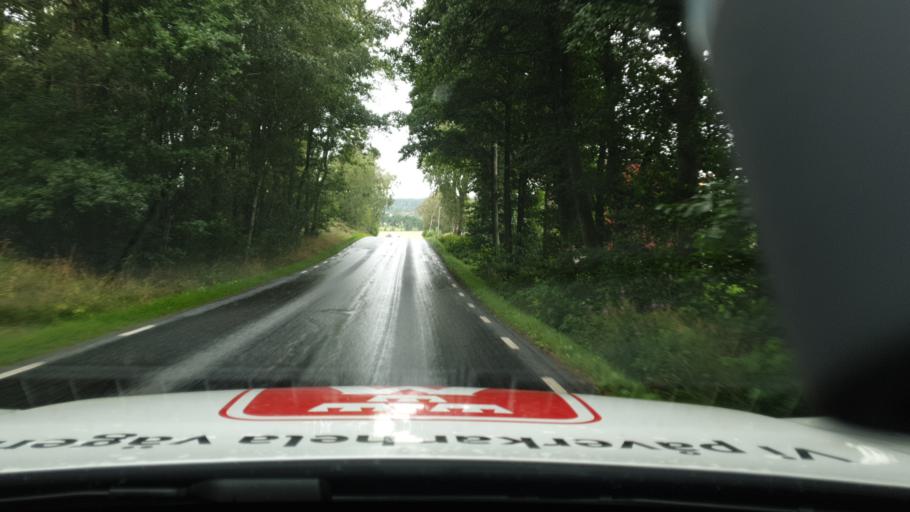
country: SE
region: Vaestra Goetaland
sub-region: Kungalvs Kommun
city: Kode
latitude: 57.9051
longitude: 11.8047
